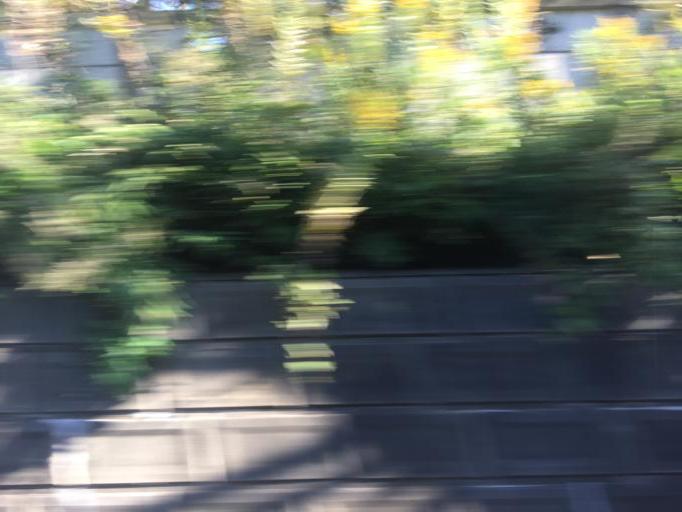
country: JP
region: Chiba
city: Funabashi
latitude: 35.7096
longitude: 139.9662
